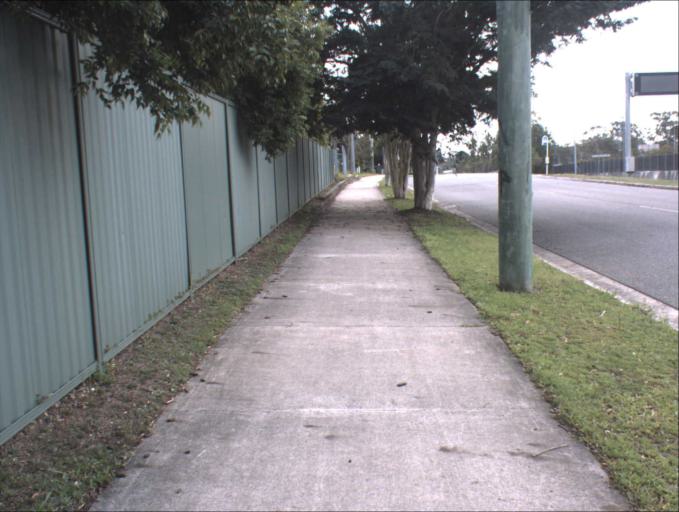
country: AU
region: Queensland
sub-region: Logan
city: Park Ridge South
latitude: -27.6930
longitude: 153.0348
